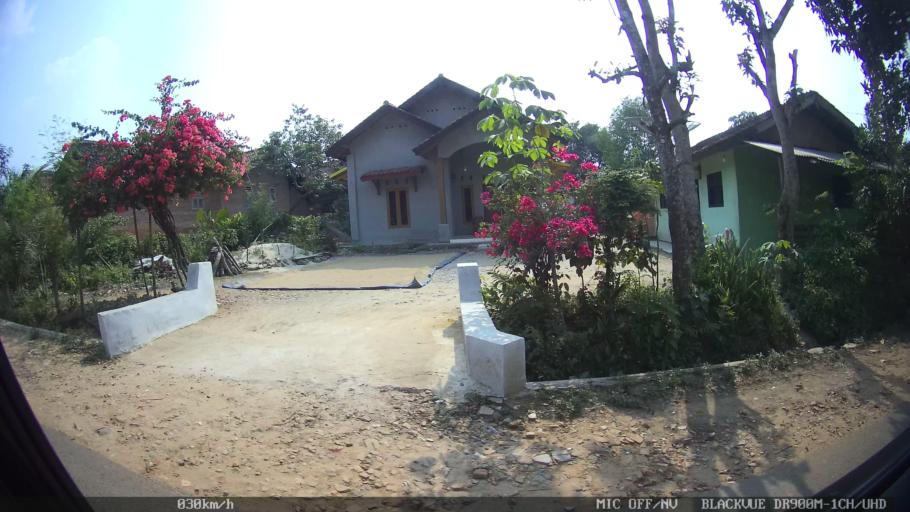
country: ID
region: Lampung
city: Pringsewu
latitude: -5.3967
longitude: 104.9922
